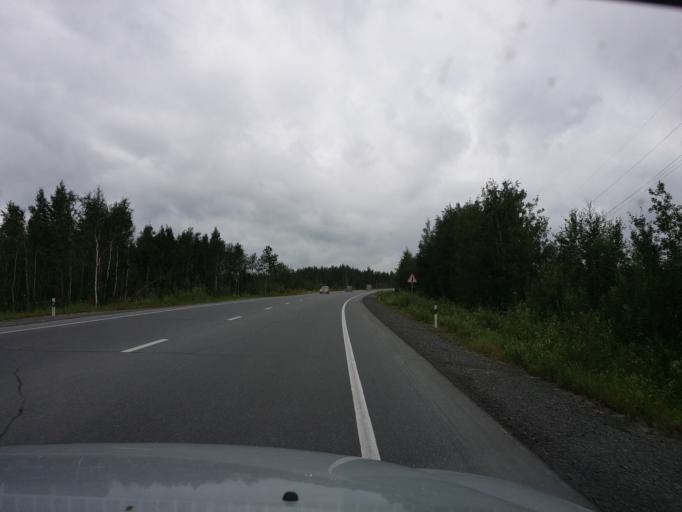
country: RU
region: Khanty-Mansiyskiy Avtonomnyy Okrug
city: Nizhnevartovsk
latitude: 61.0437
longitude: 76.3498
